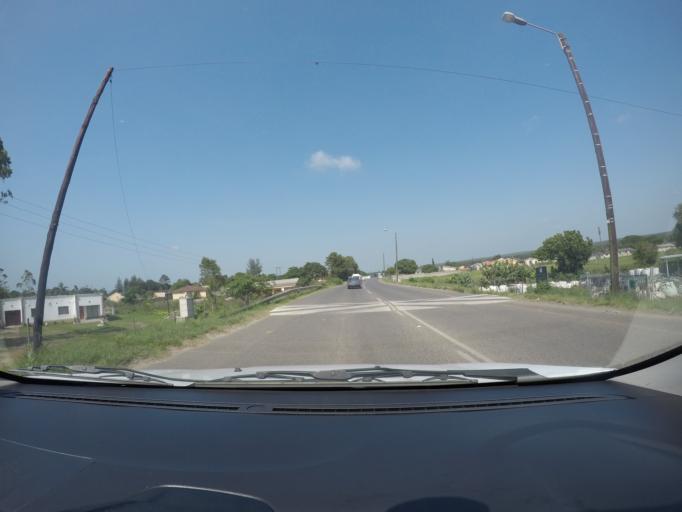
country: ZA
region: KwaZulu-Natal
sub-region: uThungulu District Municipality
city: eSikhawini
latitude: -28.8924
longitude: 31.8885
